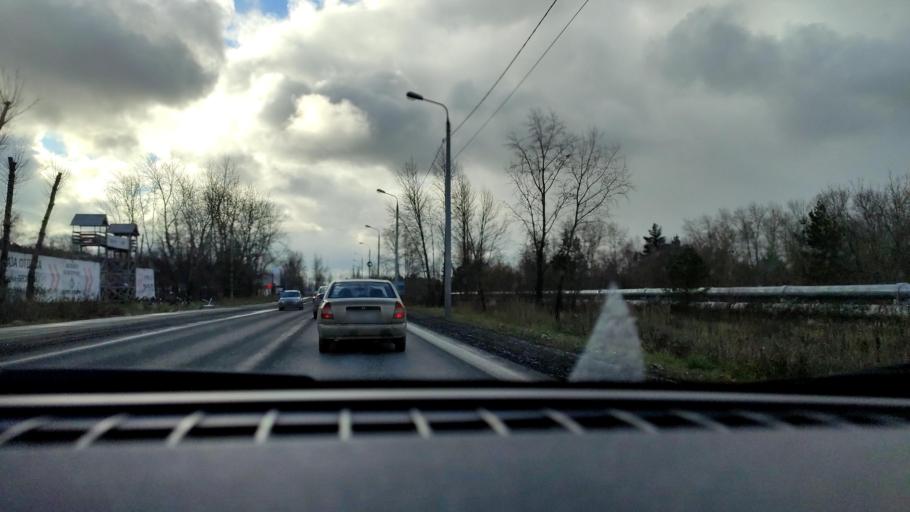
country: RU
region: Perm
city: Kondratovo
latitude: 57.9753
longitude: 56.1291
